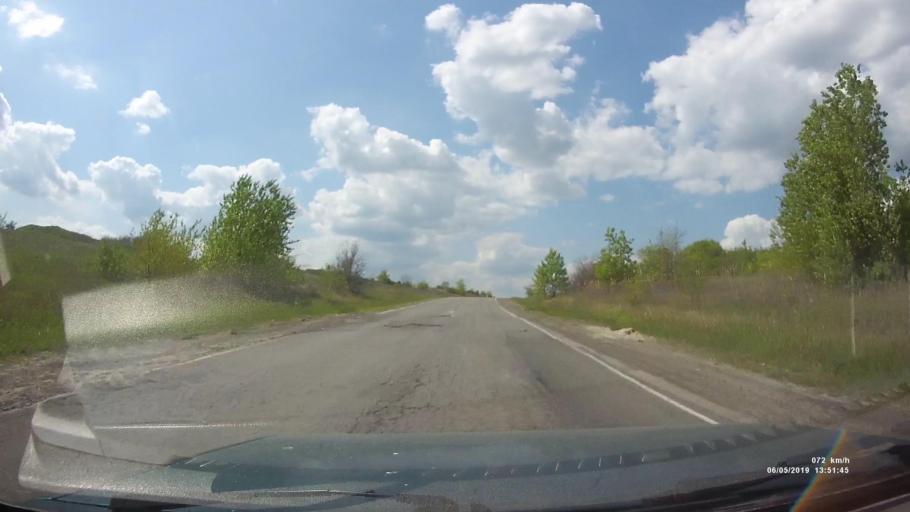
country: RU
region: Rostov
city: Melikhovskaya
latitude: 47.6583
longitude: 40.4870
